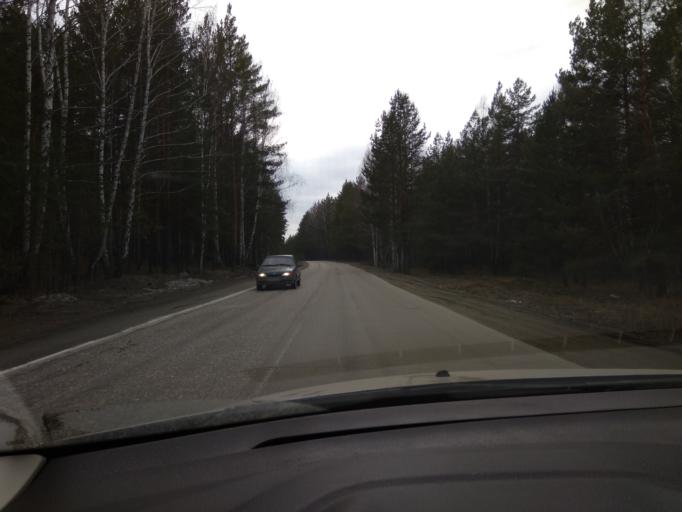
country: RU
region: Chelyabinsk
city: Kyshtym
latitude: 55.7167
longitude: 60.6227
